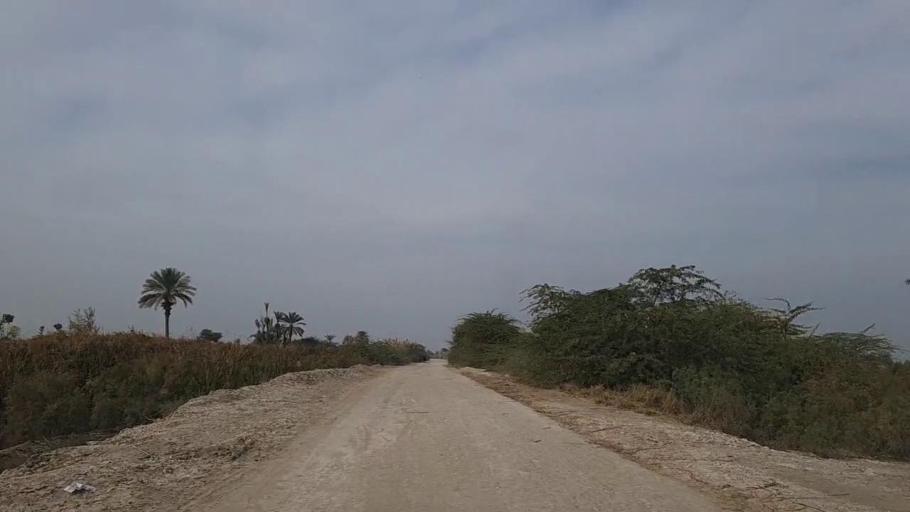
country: PK
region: Sindh
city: Daur
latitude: 26.4031
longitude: 68.4391
